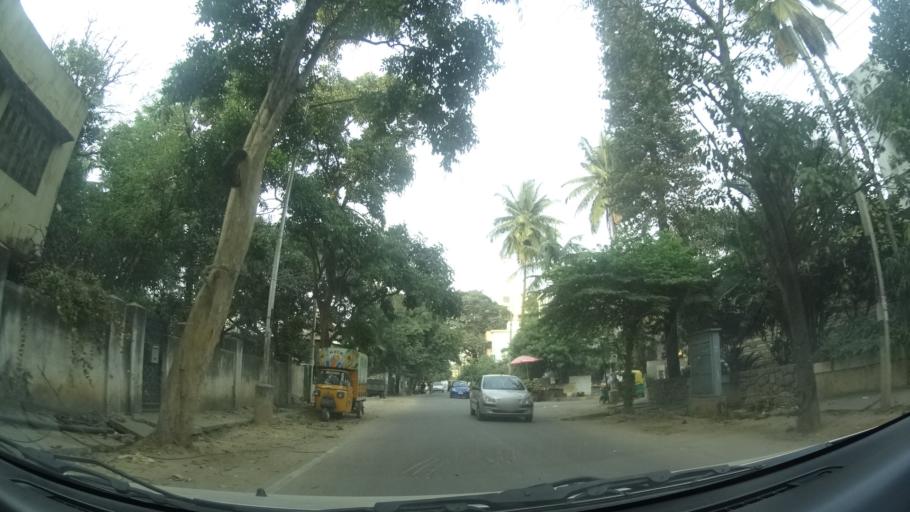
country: IN
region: Karnataka
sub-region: Bangalore Urban
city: Bangalore
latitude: 13.0017
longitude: 77.6260
